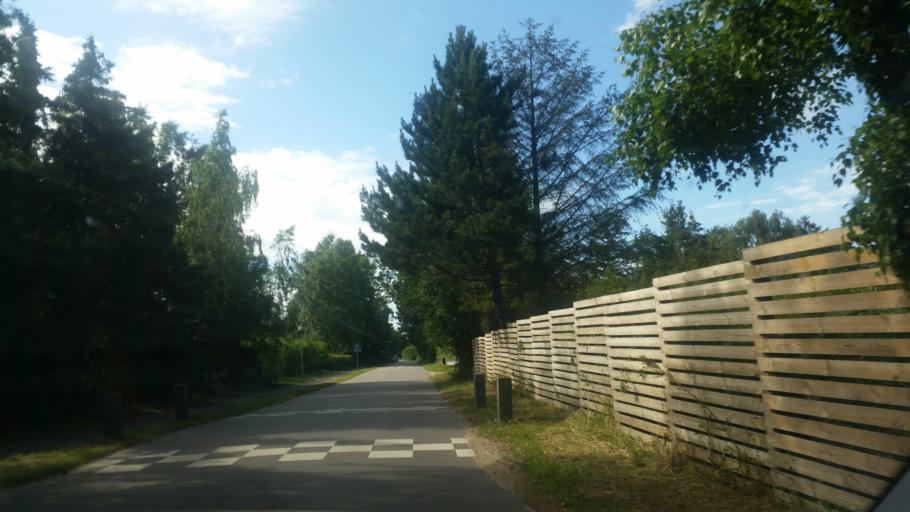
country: DK
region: Zealand
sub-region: Odsherred Kommune
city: Horve
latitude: 55.8243
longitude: 11.4014
